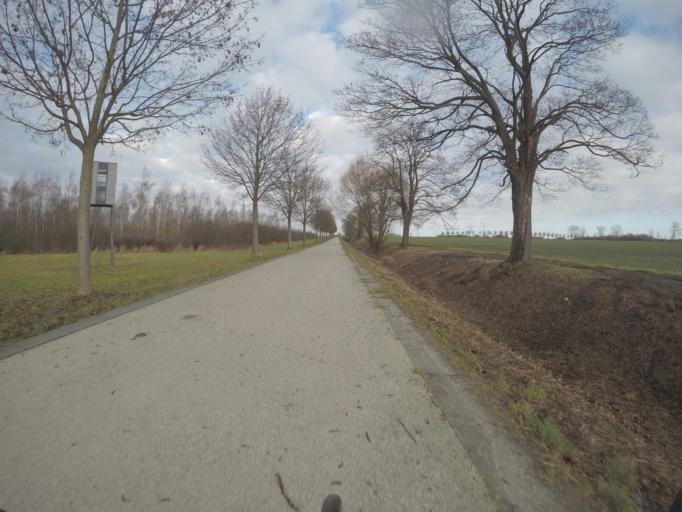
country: DE
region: Berlin
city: Wartenberg
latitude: 52.5888
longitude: 13.5047
